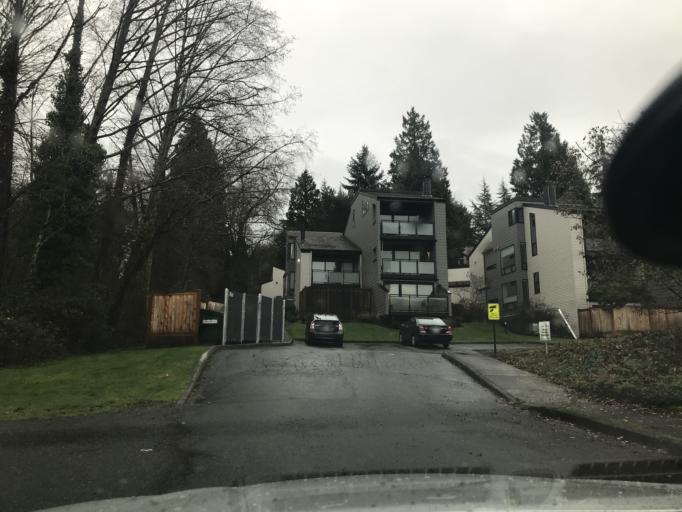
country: US
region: Washington
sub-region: King County
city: Kirkland
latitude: 47.6682
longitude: -122.1912
